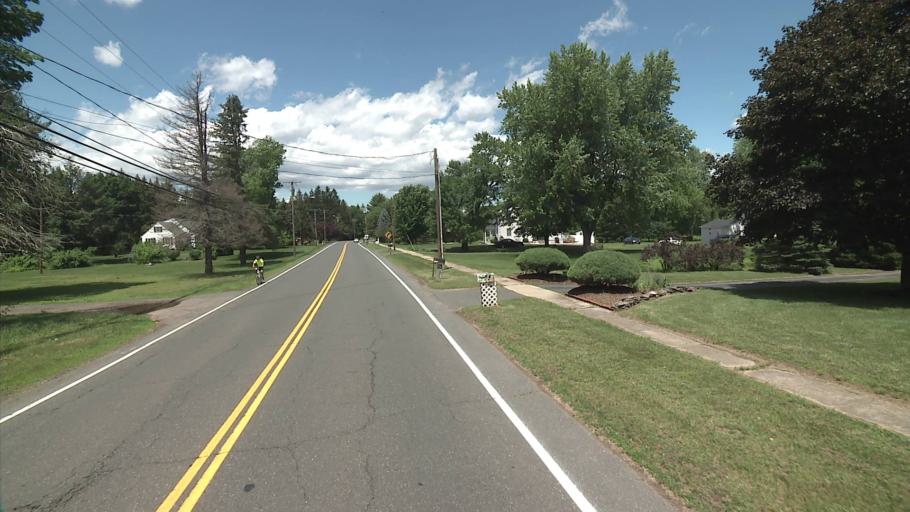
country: US
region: Connecticut
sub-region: Hartford County
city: Sherwood Manor
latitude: 42.0131
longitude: -72.5420
